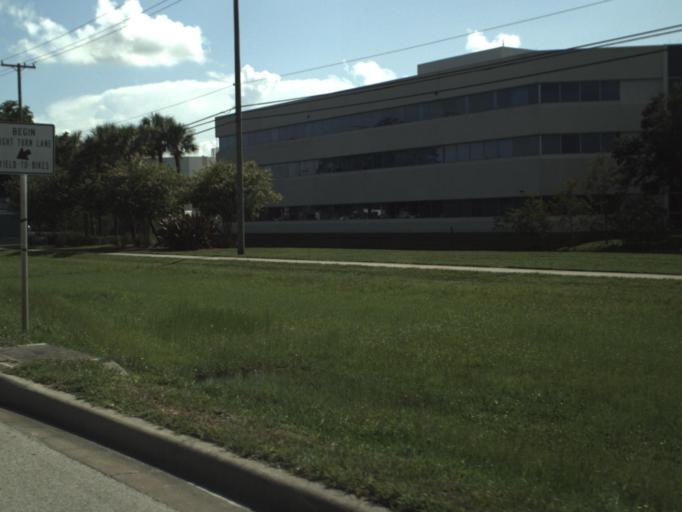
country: US
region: Florida
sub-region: Palm Beach County
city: Wellington
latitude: 26.6534
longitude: -80.2036
